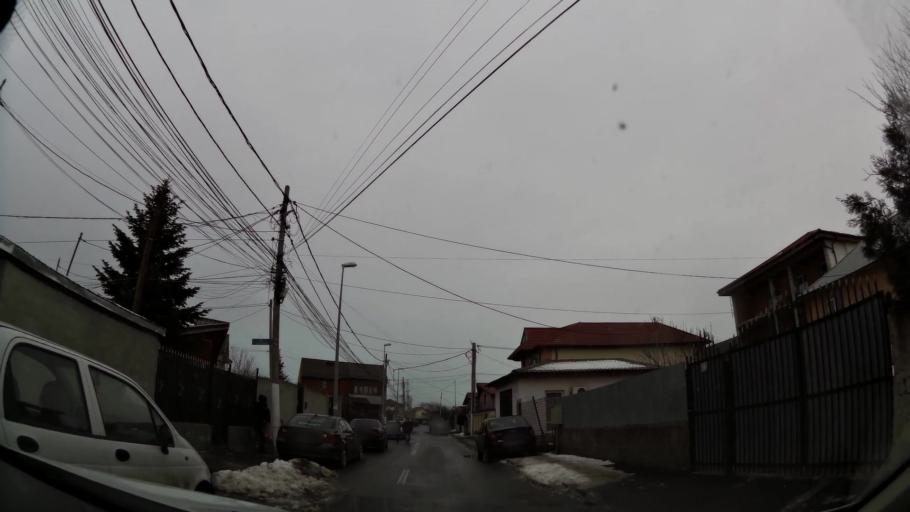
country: RO
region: Ilfov
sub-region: Comuna Pantelimon
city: Pantelimon
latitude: 44.4590
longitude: 26.2043
